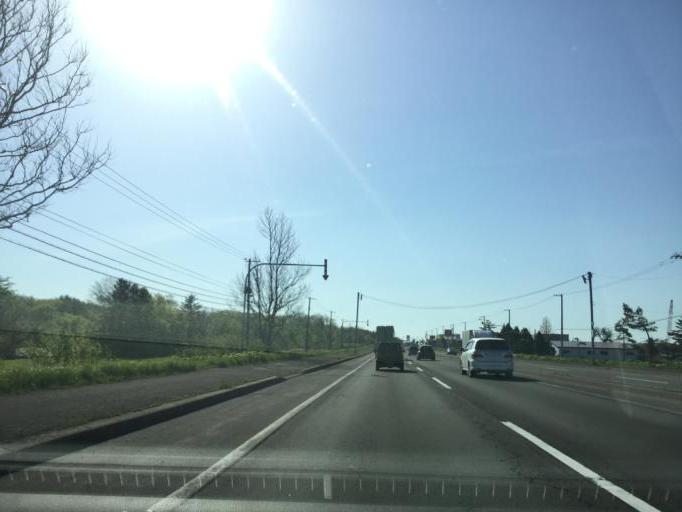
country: JP
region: Hokkaido
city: Kitahiroshima
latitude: 43.0101
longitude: 141.5144
